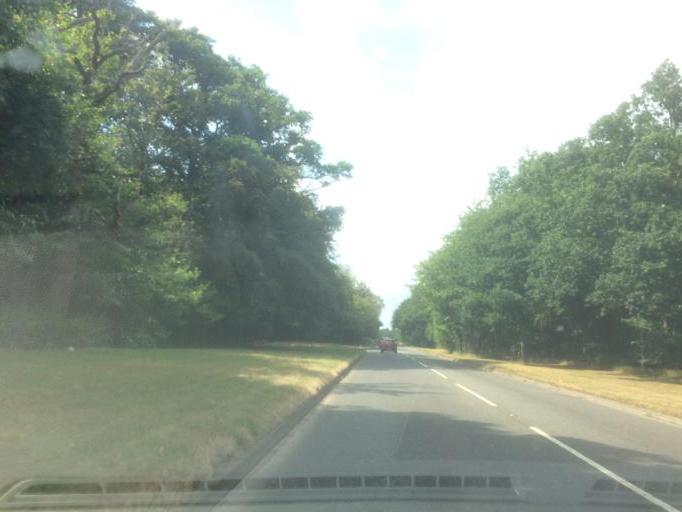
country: GB
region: England
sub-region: Buckinghamshire
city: Farnham Royal
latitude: 51.5692
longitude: -0.6184
